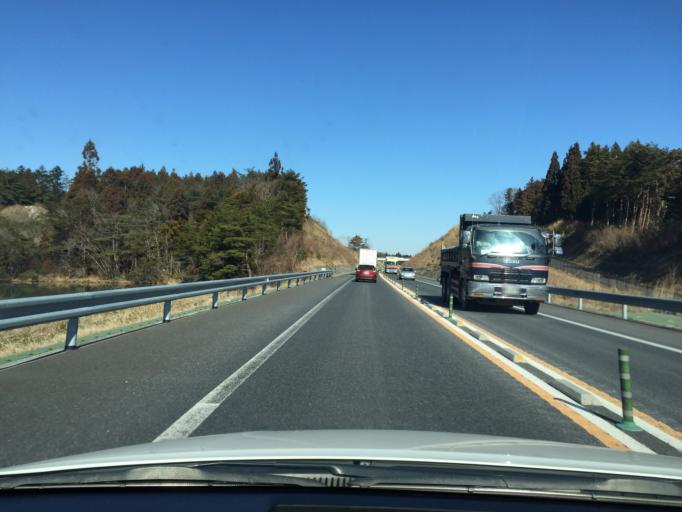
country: JP
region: Miyagi
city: Marumori
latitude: 37.7509
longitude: 140.9027
